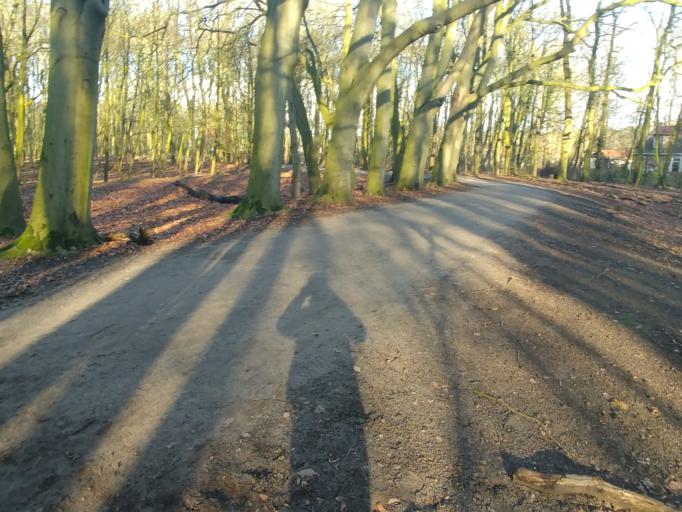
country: NL
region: North Holland
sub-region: Gemeente Bloemendaal
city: Bennebroek
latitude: 52.3444
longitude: 4.5811
